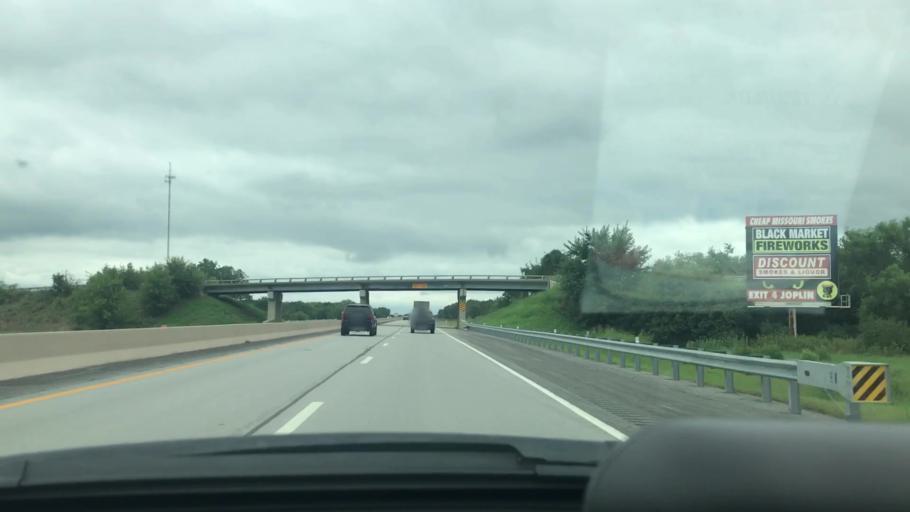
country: US
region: Oklahoma
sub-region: Ottawa County
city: Commerce
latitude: 36.9102
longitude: -94.7893
